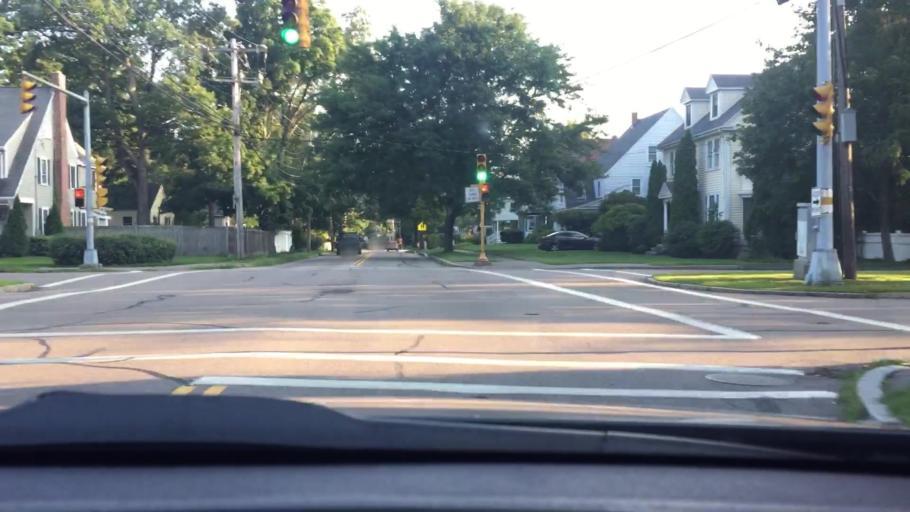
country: US
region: Massachusetts
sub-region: Norfolk County
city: Needham
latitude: 42.2779
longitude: -71.2304
